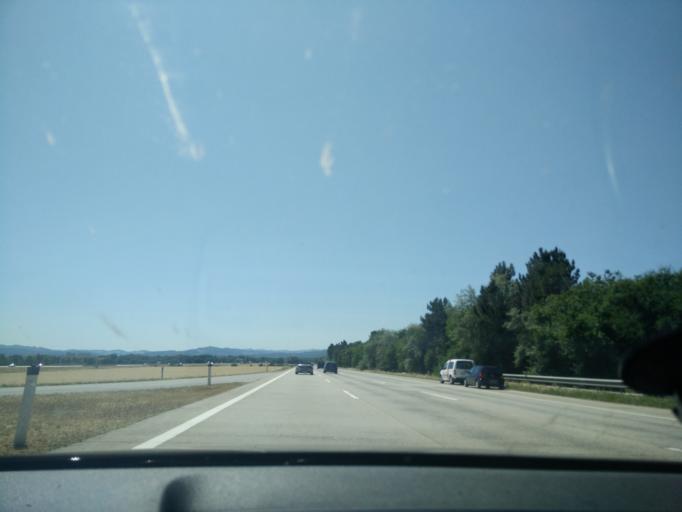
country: AT
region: Lower Austria
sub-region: Wiener Neustadt Stadt
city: Wiener Neustadt
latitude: 47.7833
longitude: 16.2040
